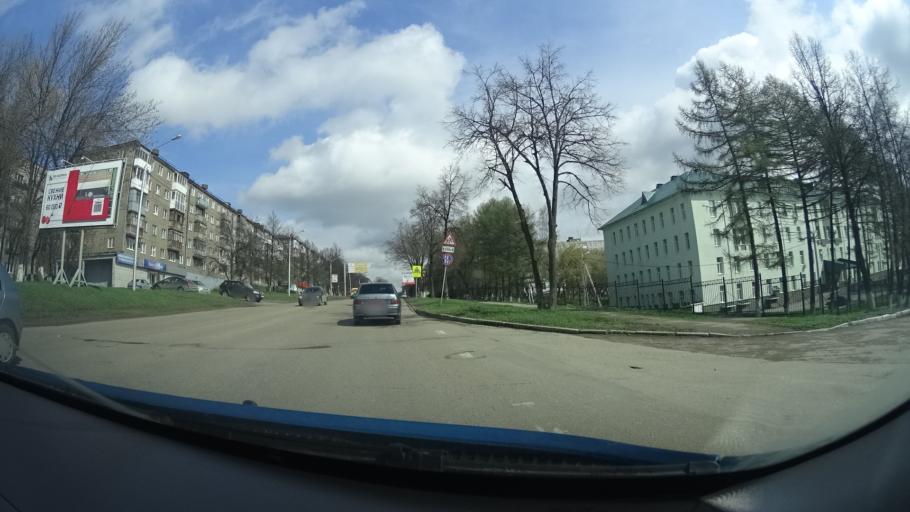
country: RU
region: Bashkortostan
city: Ufa
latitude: 54.8123
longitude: 56.0704
